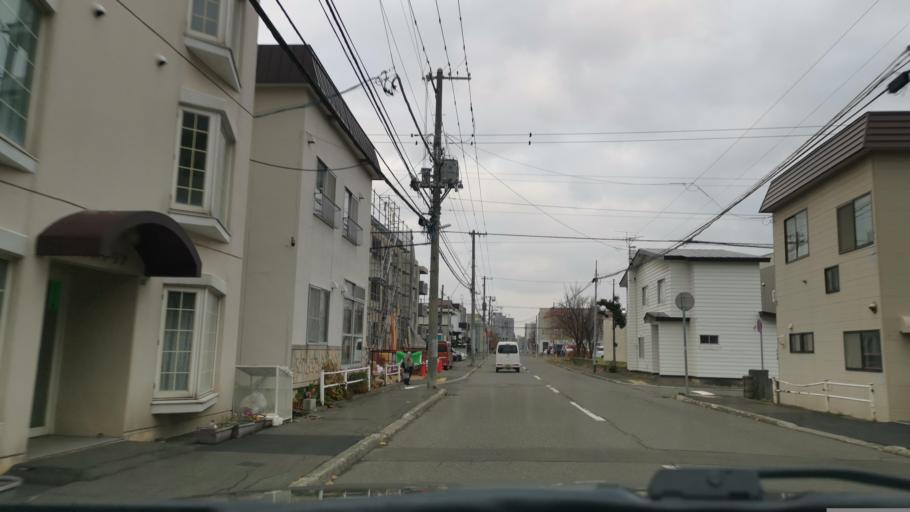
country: JP
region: Hokkaido
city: Sapporo
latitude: 43.0399
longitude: 141.4155
